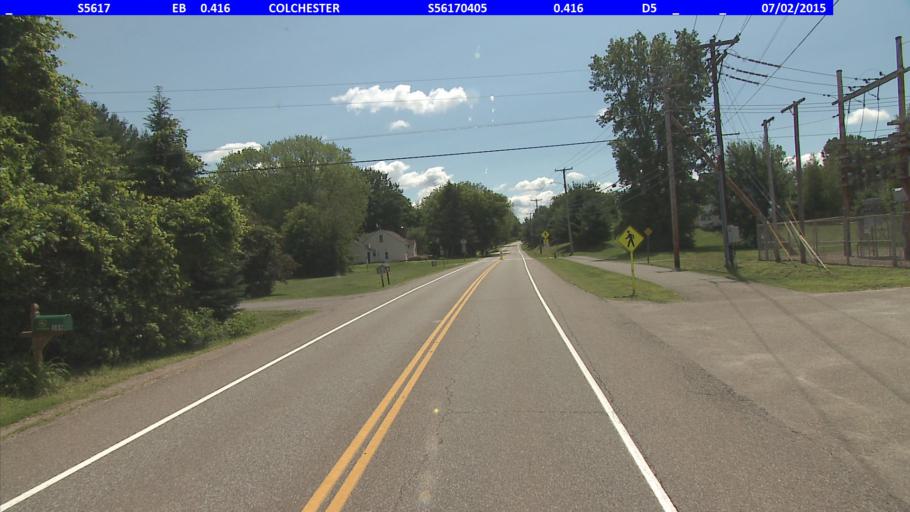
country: US
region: Vermont
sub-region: Chittenden County
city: Colchester
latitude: 44.5540
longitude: -73.1826
